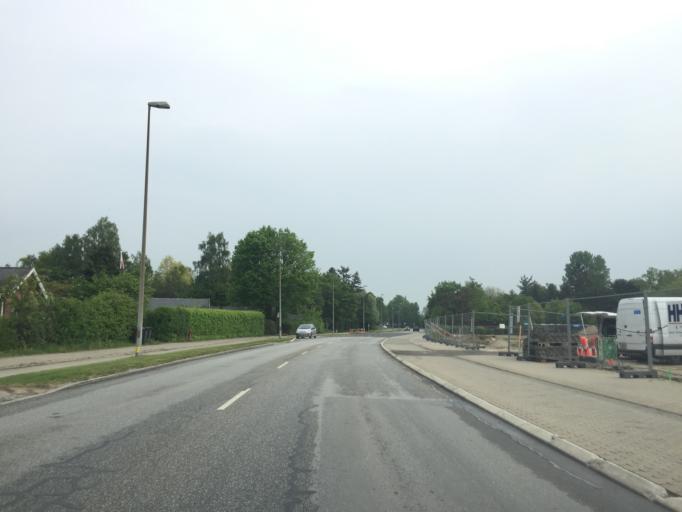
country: DK
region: Capital Region
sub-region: Rodovre Kommune
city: Rodovre
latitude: 55.6776
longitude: 12.4337
